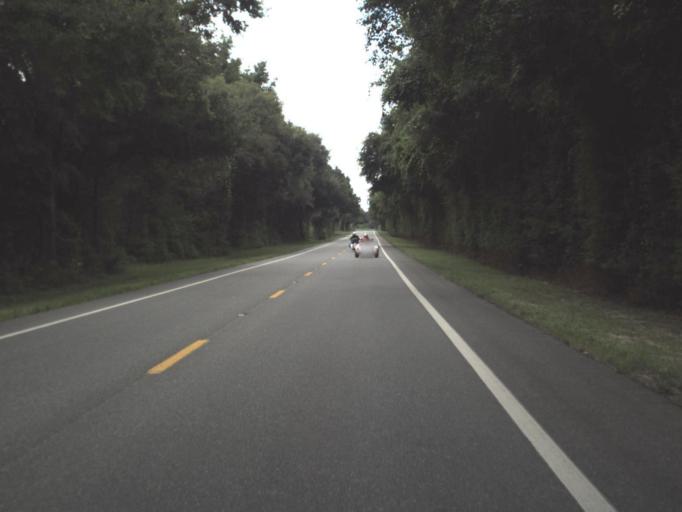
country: US
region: Florida
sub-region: Alachua County
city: Newberry
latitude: 29.5903
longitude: -82.5615
